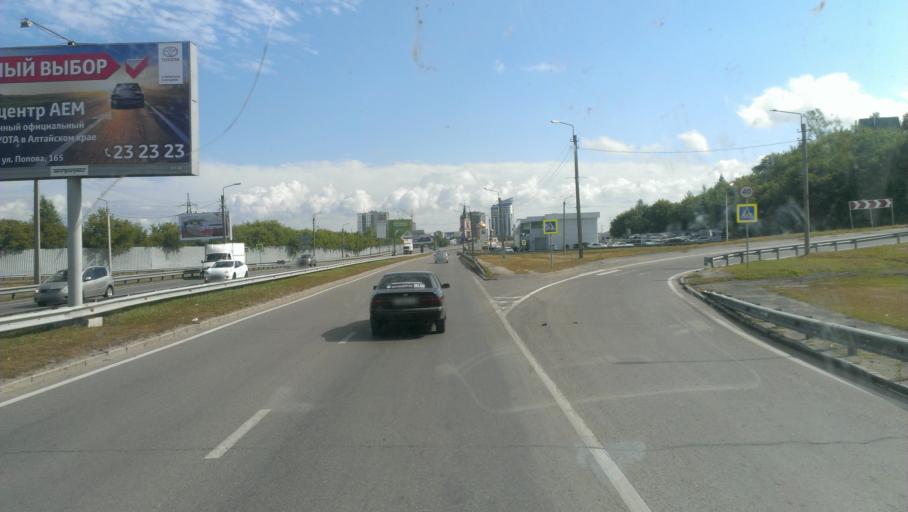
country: RU
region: Altai Krai
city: Zaton
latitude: 53.3240
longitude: 83.7889
